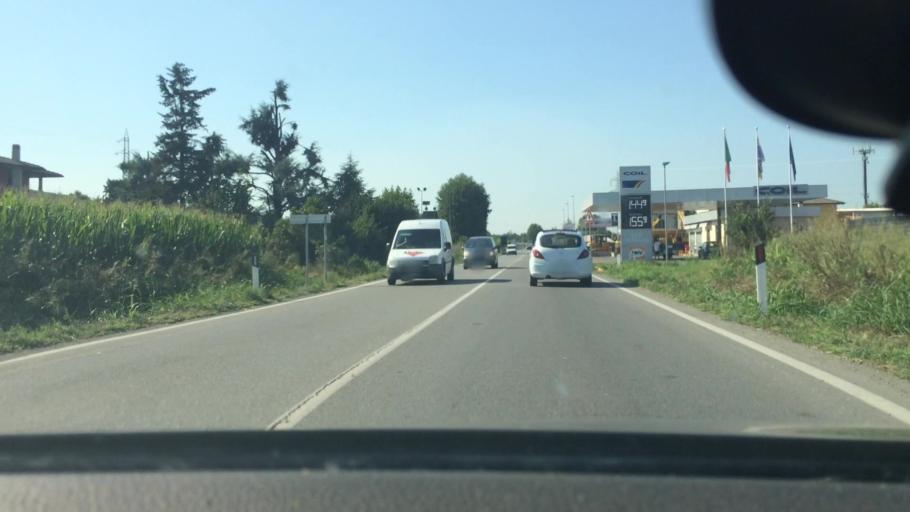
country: IT
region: Lombardy
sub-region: Provincia di Lodi
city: Guardamiglio
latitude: 45.0979
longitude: 9.6873
